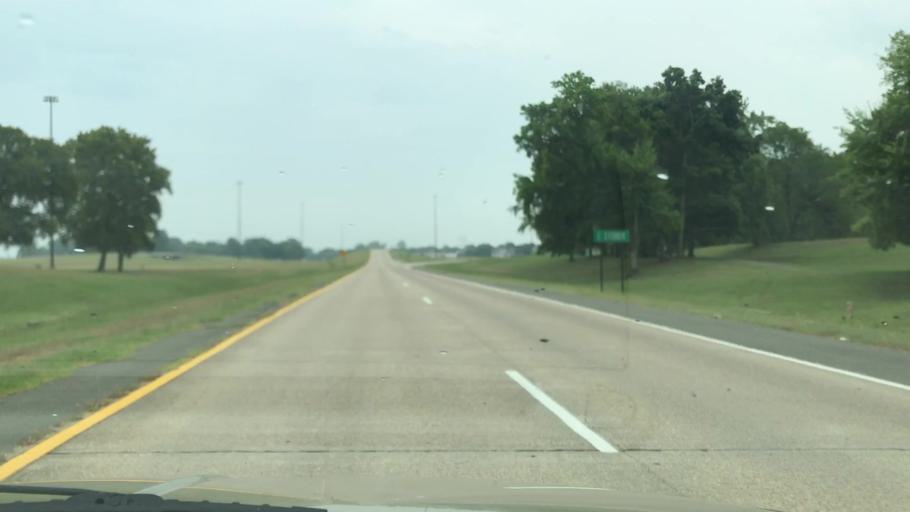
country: US
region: Louisiana
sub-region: Bossier Parish
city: Bossier City
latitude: 32.5035
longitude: -93.7196
